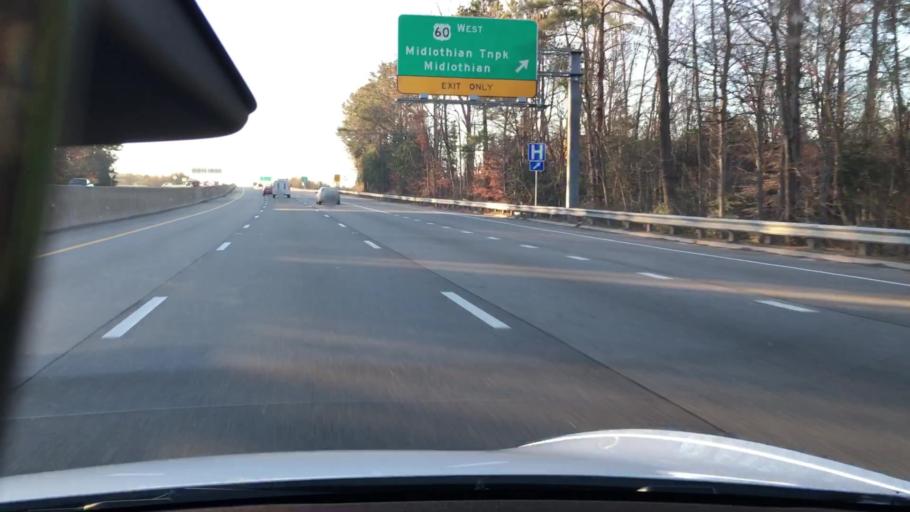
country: US
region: Virginia
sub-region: Chesterfield County
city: Bon Air
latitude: 37.5056
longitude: -77.5266
